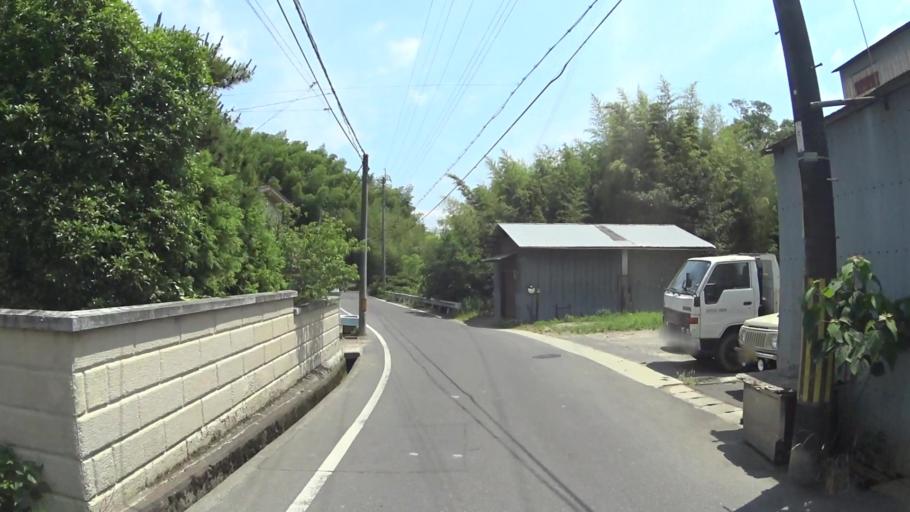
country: JP
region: Kyoto
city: Muko
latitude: 34.9444
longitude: 135.6594
